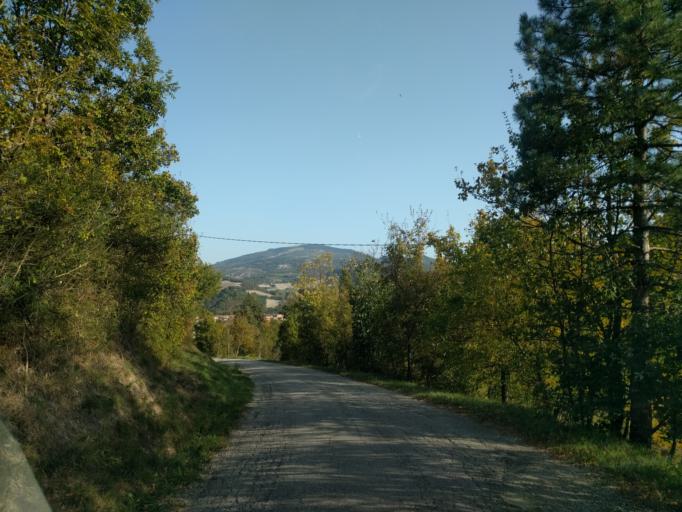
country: IT
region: The Marches
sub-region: Provincia di Pesaro e Urbino
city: Fermignano
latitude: 43.6871
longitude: 12.6344
